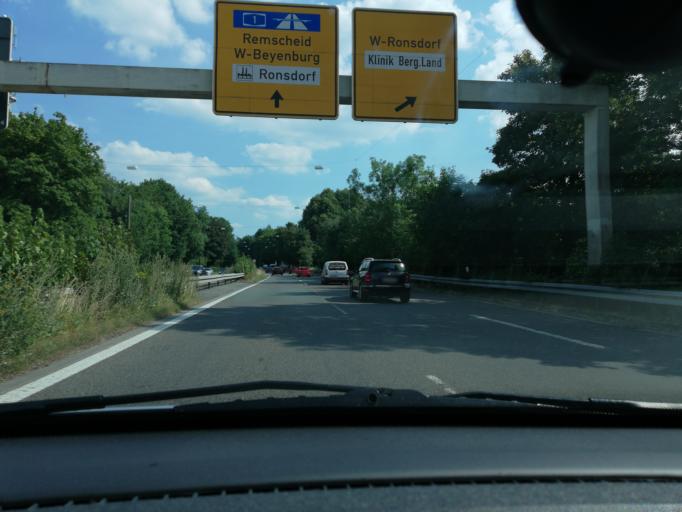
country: DE
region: North Rhine-Westphalia
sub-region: Regierungsbezirk Dusseldorf
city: Wuppertal
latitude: 51.2409
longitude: 7.1921
